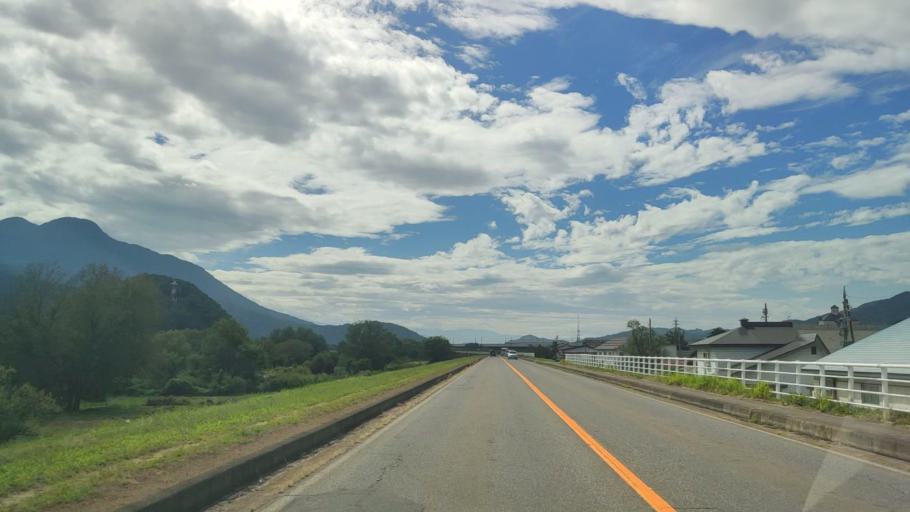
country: JP
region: Nagano
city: Iiyama
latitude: 36.8479
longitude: 138.3651
